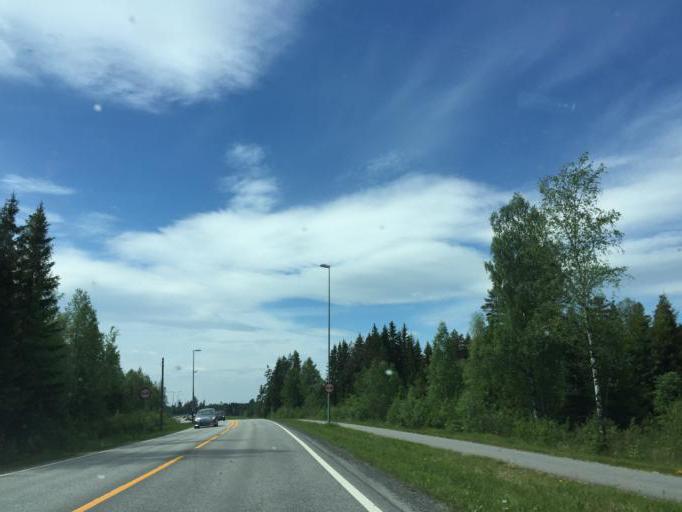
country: NO
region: Akershus
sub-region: Nes
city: Arnes
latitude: 60.1855
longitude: 11.5341
